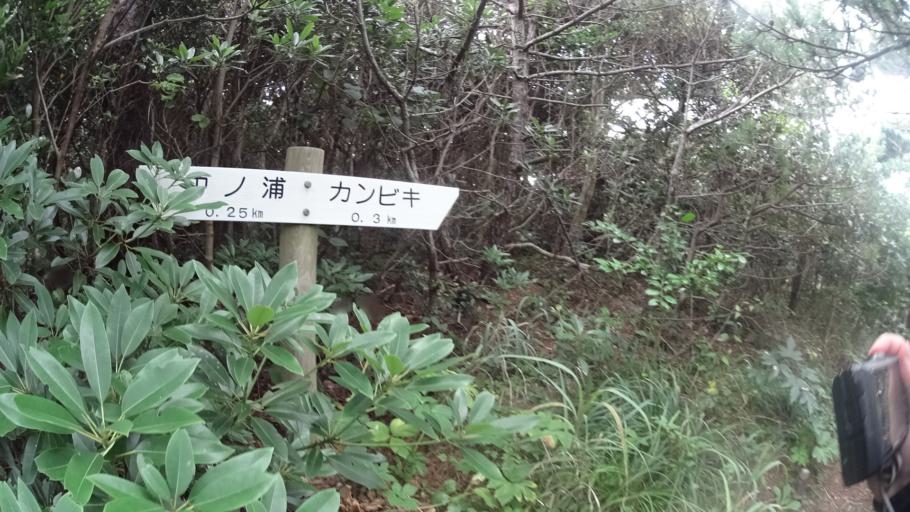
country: JP
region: Shizuoka
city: Shimoda
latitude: 34.3267
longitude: 139.2066
